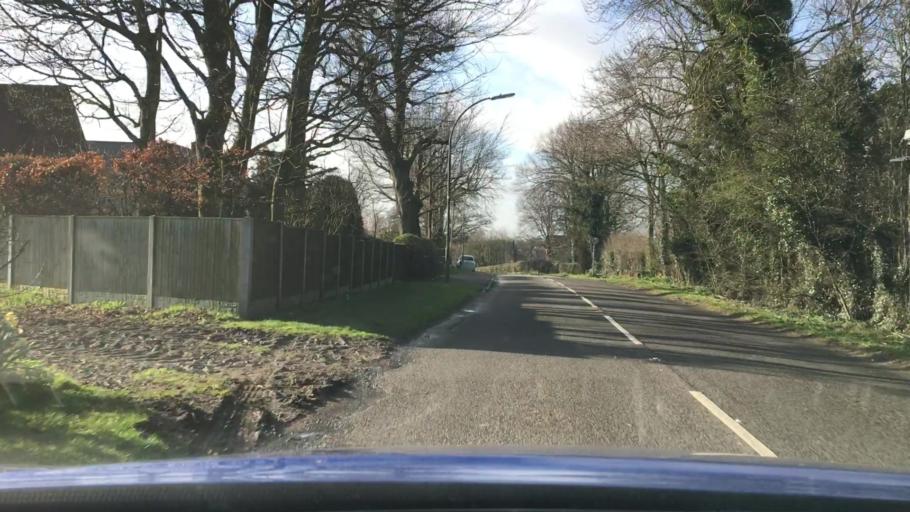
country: GB
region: England
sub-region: Derbyshire
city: Tibshelf
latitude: 53.1530
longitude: -1.3374
